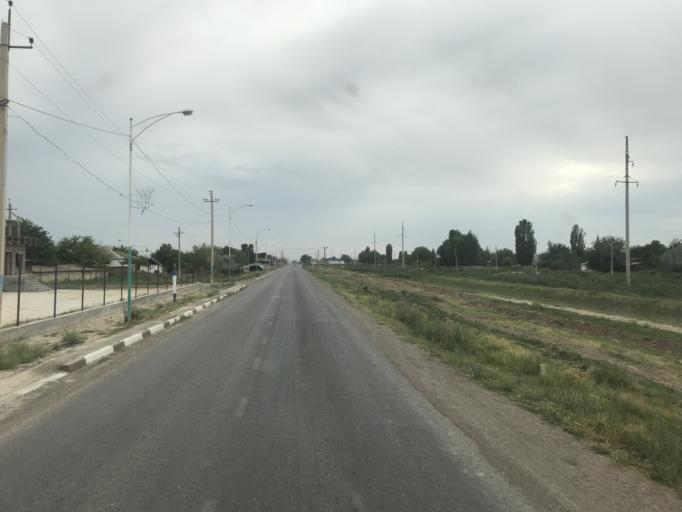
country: KZ
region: Ongtustik Qazaqstan
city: Asykata
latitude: 40.9056
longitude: 68.3655
